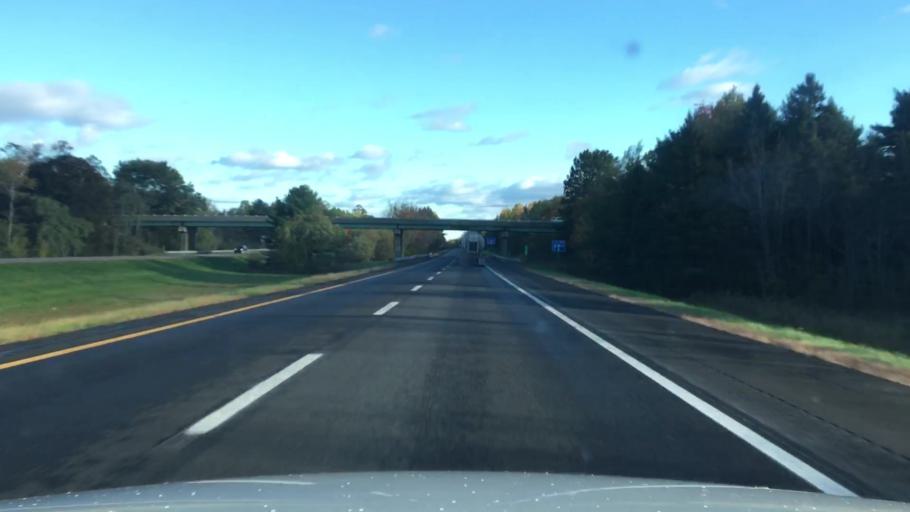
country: US
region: Maine
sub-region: Penobscot County
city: Orono
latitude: 44.8882
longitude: -68.6937
